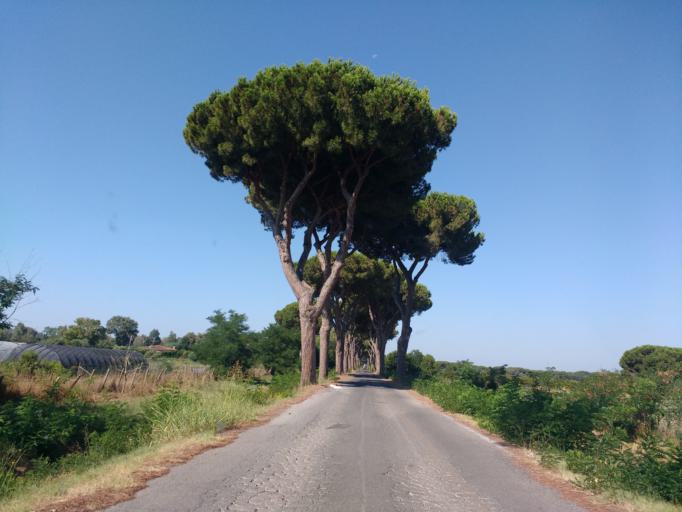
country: IT
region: Latium
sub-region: Citta metropolitana di Roma Capitale
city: Acilia-Castel Fusano-Ostia Antica
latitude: 41.7569
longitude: 12.3480
